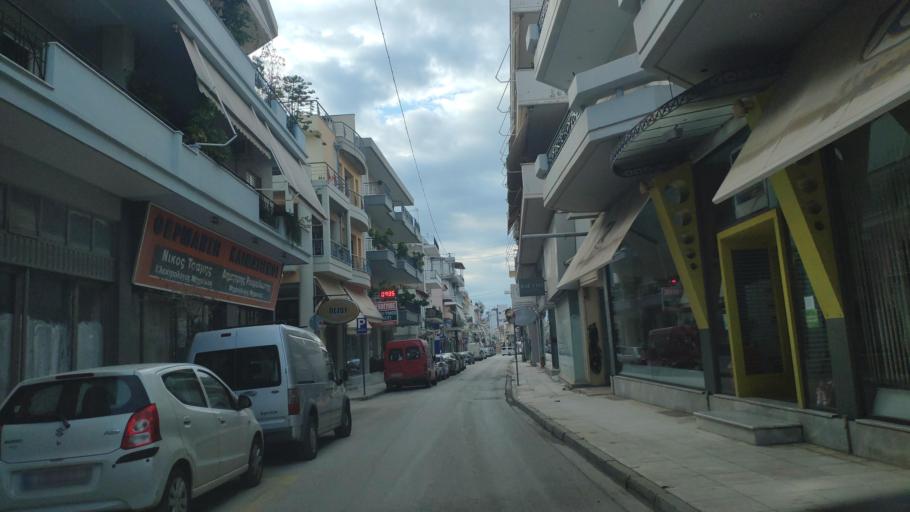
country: GR
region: Peloponnese
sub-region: Nomos Argolidos
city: Argos
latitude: 37.6381
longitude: 22.7289
